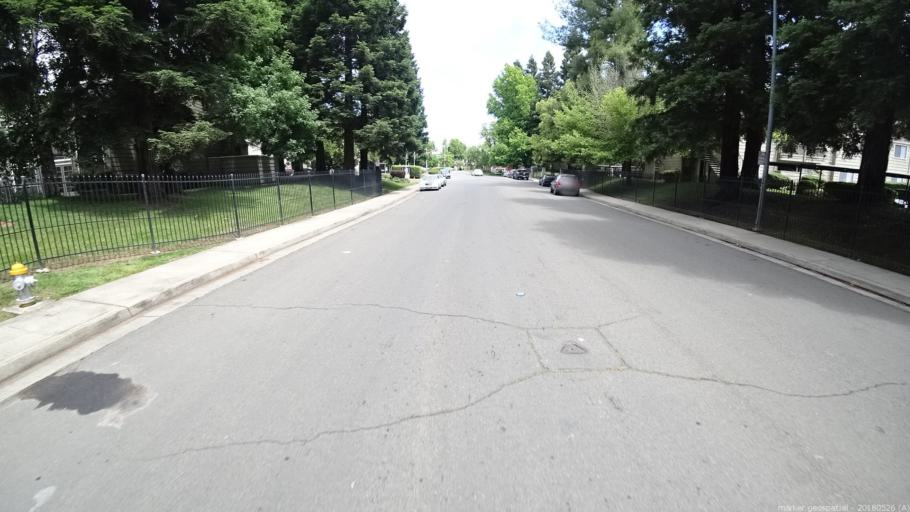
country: US
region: California
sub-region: Sacramento County
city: Sacramento
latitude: 38.6117
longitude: -121.5019
